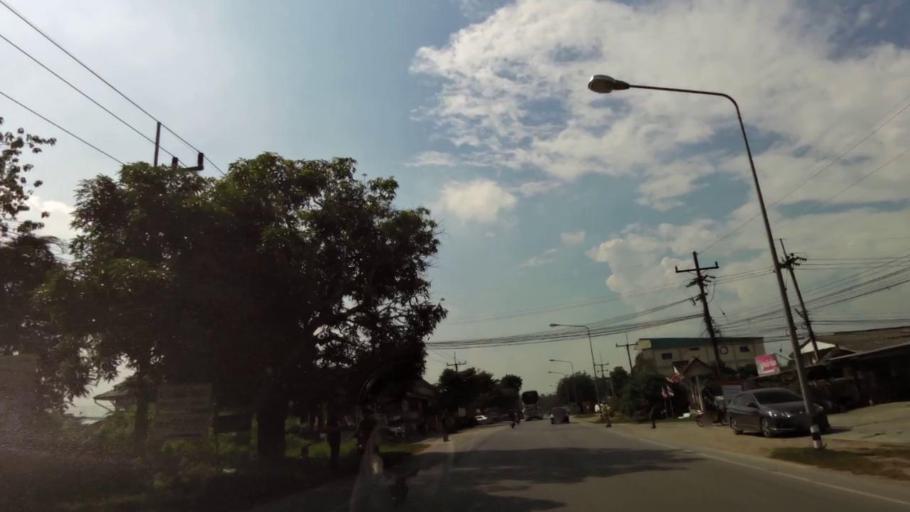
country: TH
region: Chiang Rai
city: Chiang Rai
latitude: 19.8585
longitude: 99.7622
